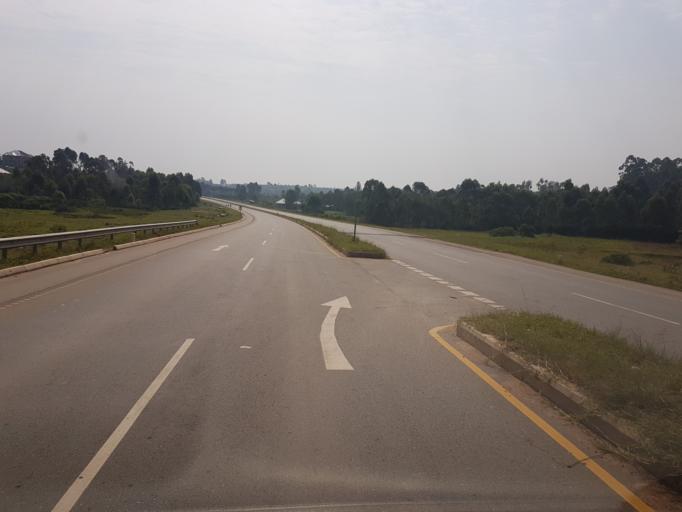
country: UG
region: Western Region
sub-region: Mbarara District
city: Bwizibwera
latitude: -0.6376
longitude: 30.5944
